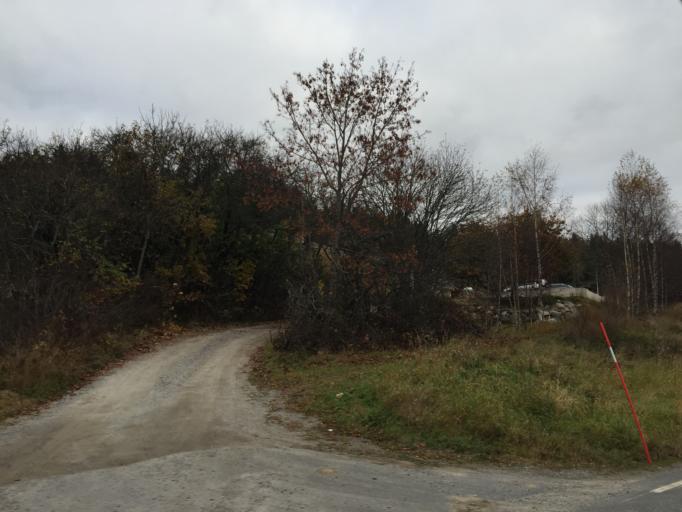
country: SE
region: Stockholm
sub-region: Sodertalje Kommun
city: Soedertaelje
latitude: 59.2464
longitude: 17.6512
